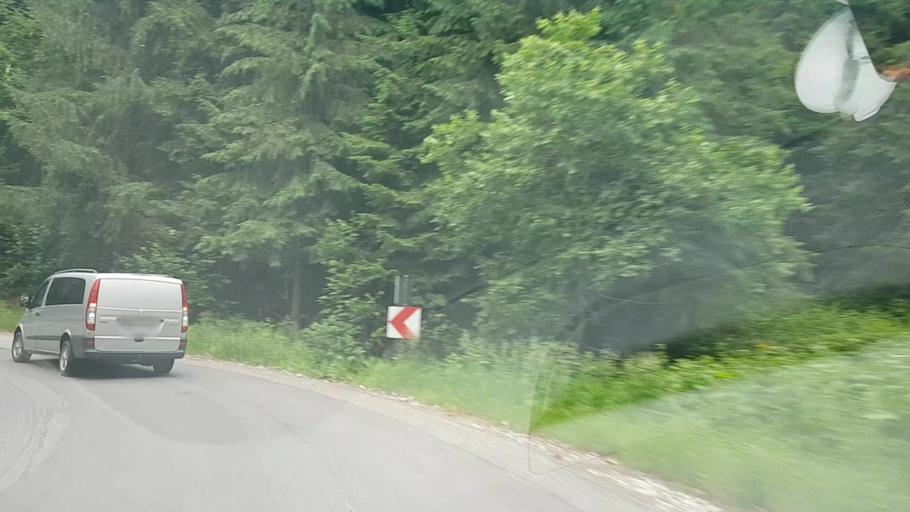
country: RO
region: Harghita
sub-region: Comuna Remetea
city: Remetea
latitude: 46.6735
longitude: 25.3496
